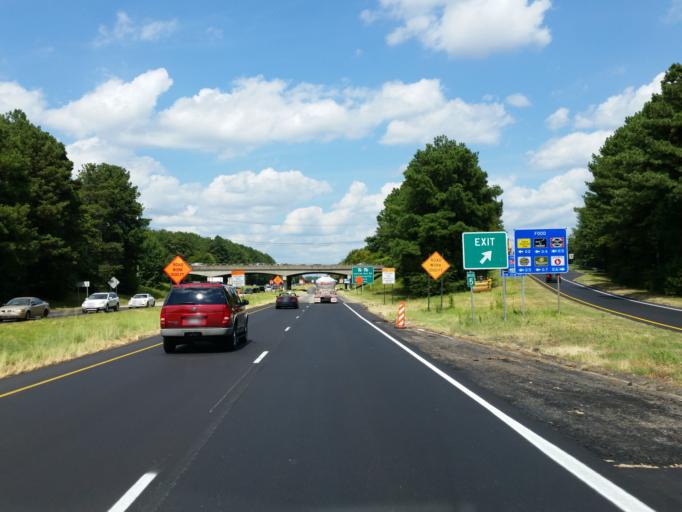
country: US
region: Georgia
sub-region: Gwinnett County
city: Lawrenceville
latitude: 33.9661
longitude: -84.0182
